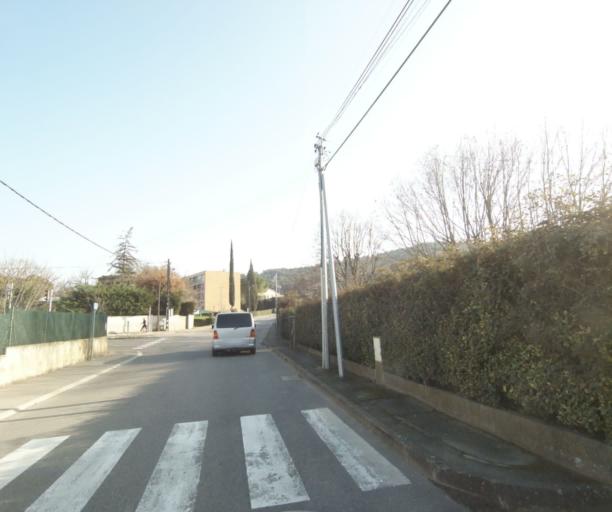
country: FR
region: Provence-Alpes-Cote d'Azur
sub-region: Departement des Bouches-du-Rhone
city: Les Pennes-Mirabeau
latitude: 43.4154
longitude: 5.2999
